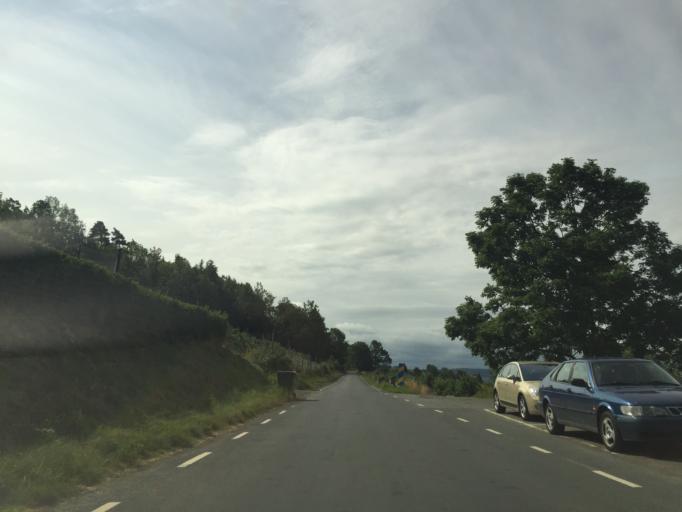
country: SE
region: Joenkoeping
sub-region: Jonkopings Kommun
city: Kaxholmen
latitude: 57.8432
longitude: 14.2707
